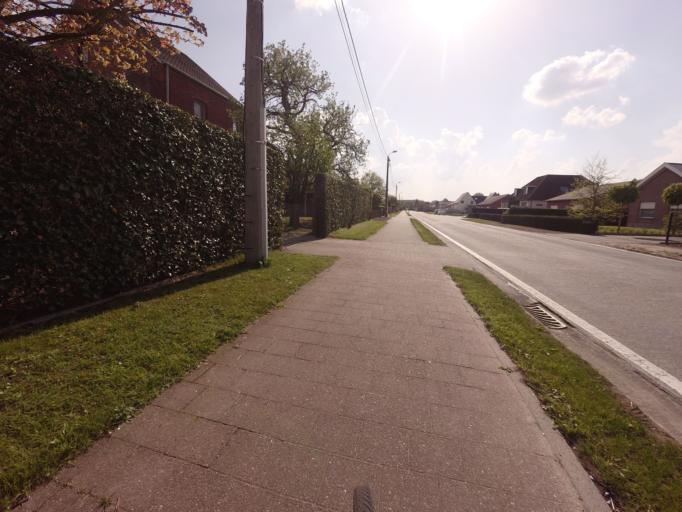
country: BE
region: Flanders
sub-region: Provincie Antwerpen
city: Putte
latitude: 51.0724
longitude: 4.6553
